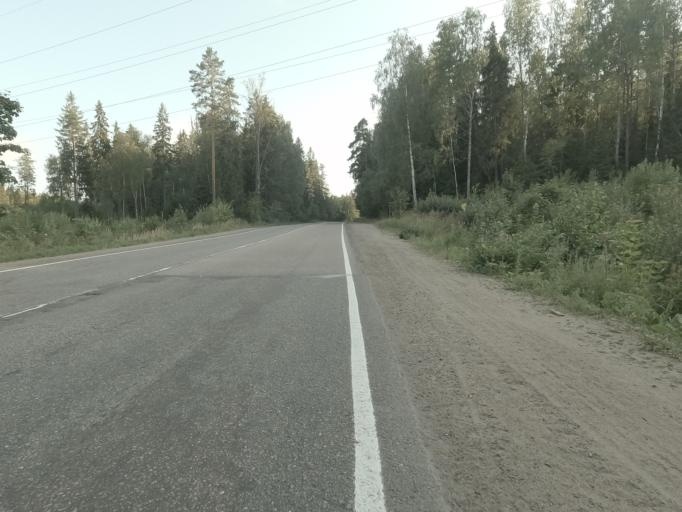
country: RU
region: Leningrad
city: Vyborg
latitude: 60.7447
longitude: 28.7693
